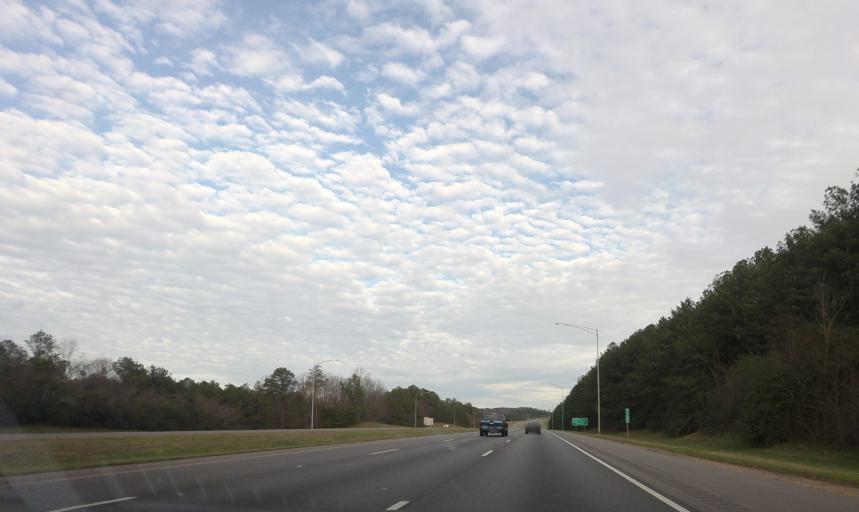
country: US
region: Alabama
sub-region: Jefferson County
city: Irondale
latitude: 33.5436
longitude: -86.6779
